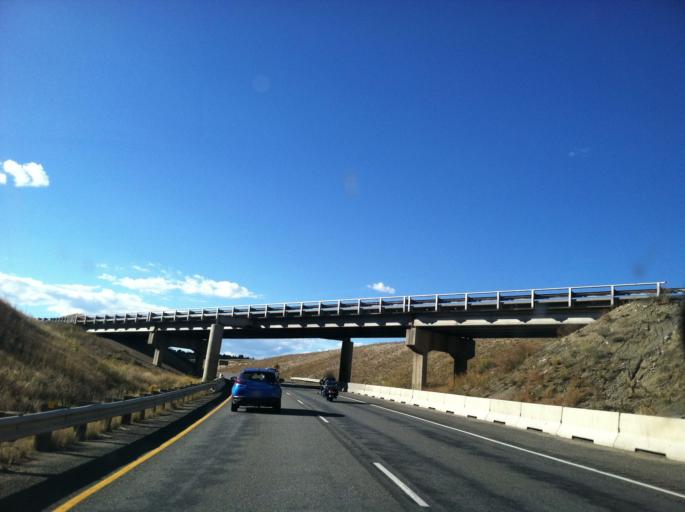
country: US
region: Montana
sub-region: Silver Bow County
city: Butte
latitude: 46.0035
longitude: -112.5694
